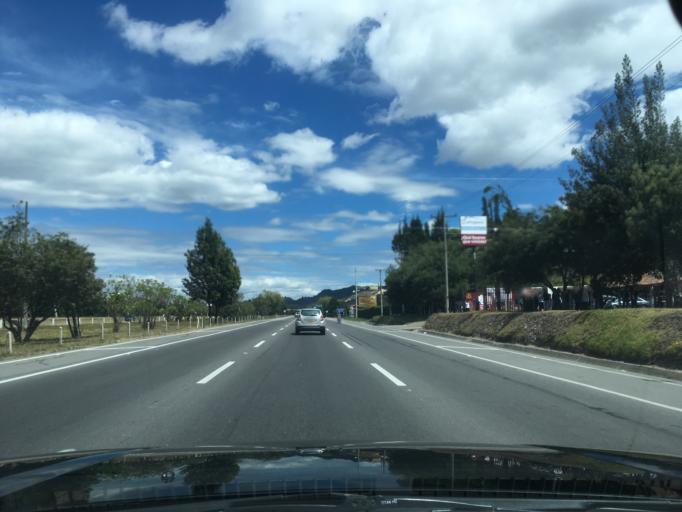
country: CO
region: Cundinamarca
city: Cajica
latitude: 4.8806
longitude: -74.0169
